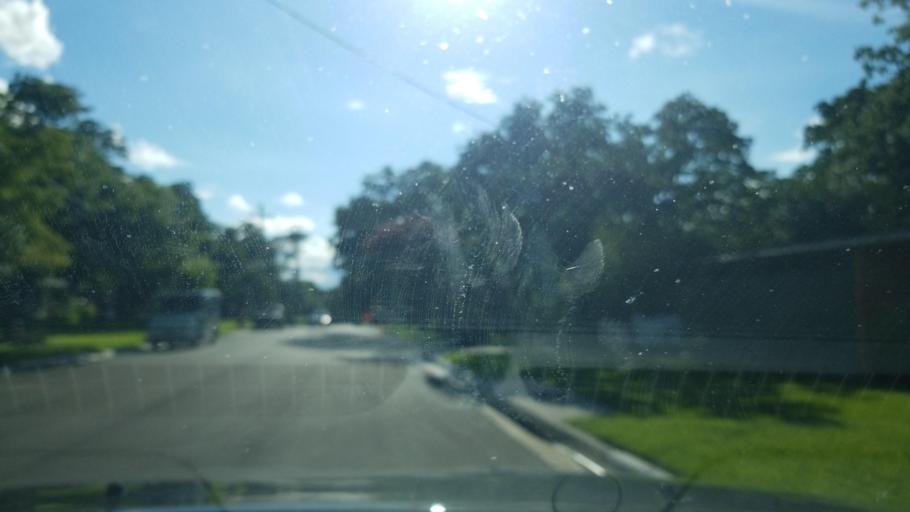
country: US
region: Texas
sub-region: Denton County
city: Denton
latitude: 33.2372
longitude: -97.1109
